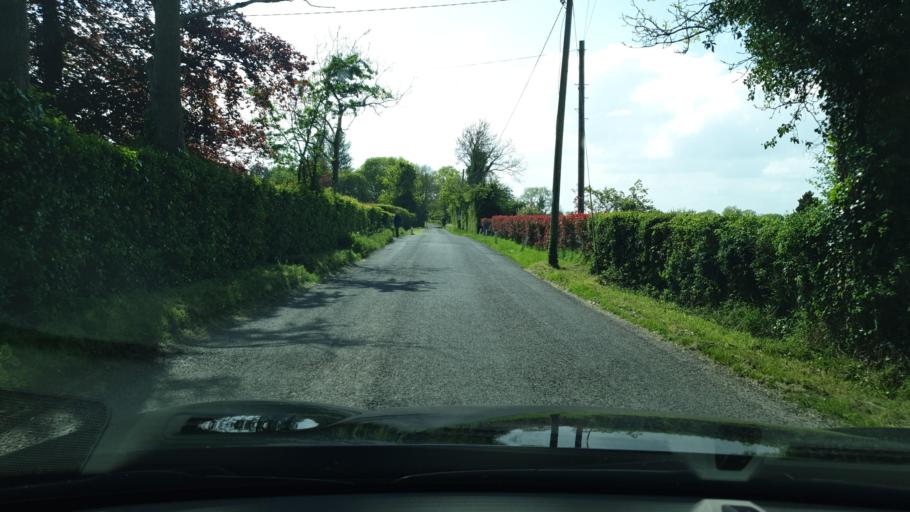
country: IE
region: Leinster
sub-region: Kildare
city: Maynooth
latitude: 53.4340
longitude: -6.5672
